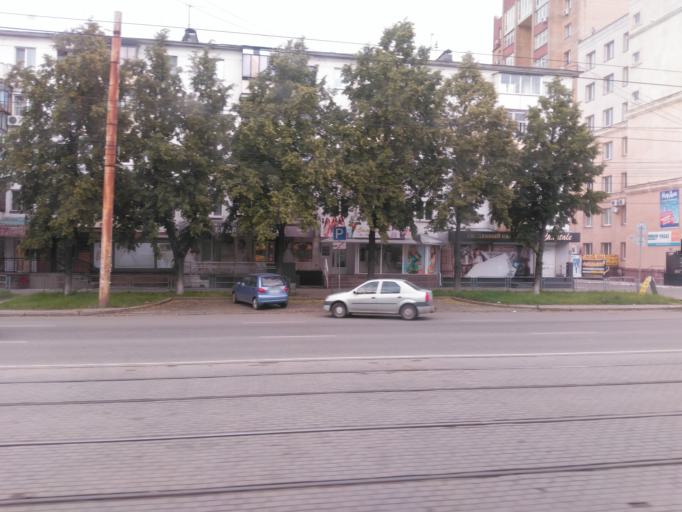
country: RU
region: Chelyabinsk
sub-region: Gorod Chelyabinsk
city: Chelyabinsk
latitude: 55.1817
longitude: 61.3989
